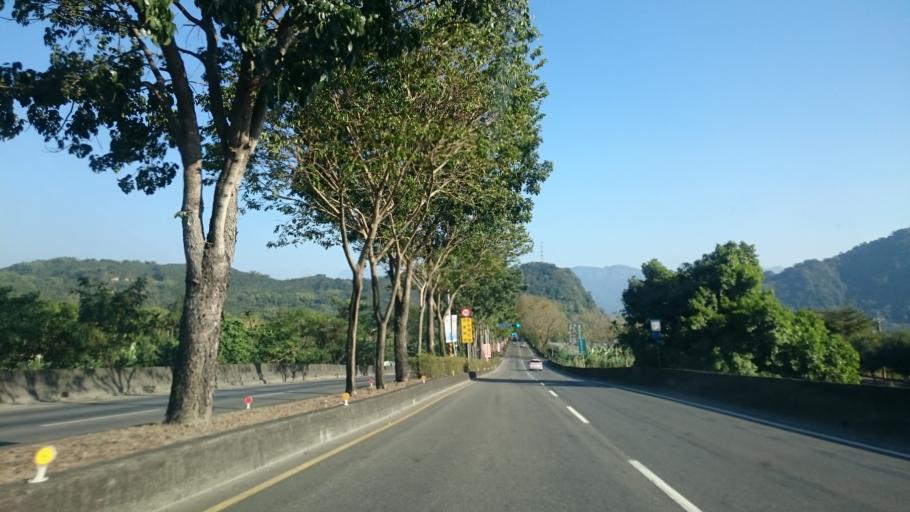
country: TW
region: Taiwan
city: Lugu
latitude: 23.8293
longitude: 120.7509
